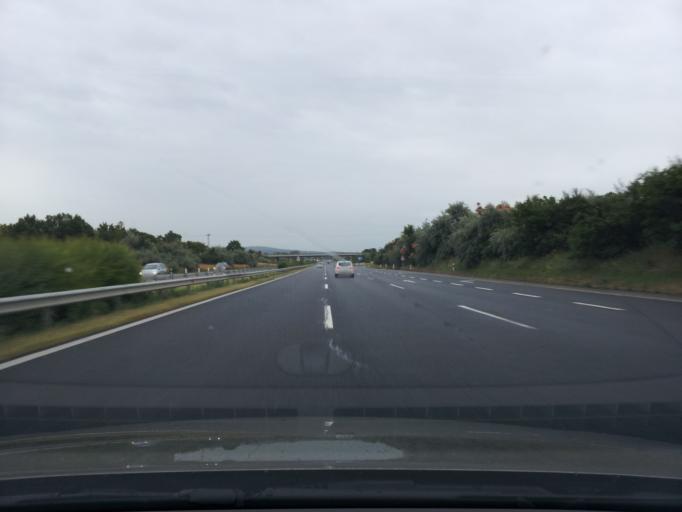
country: HU
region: Fejer
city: Pakozd
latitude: 47.1905
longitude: 18.5048
